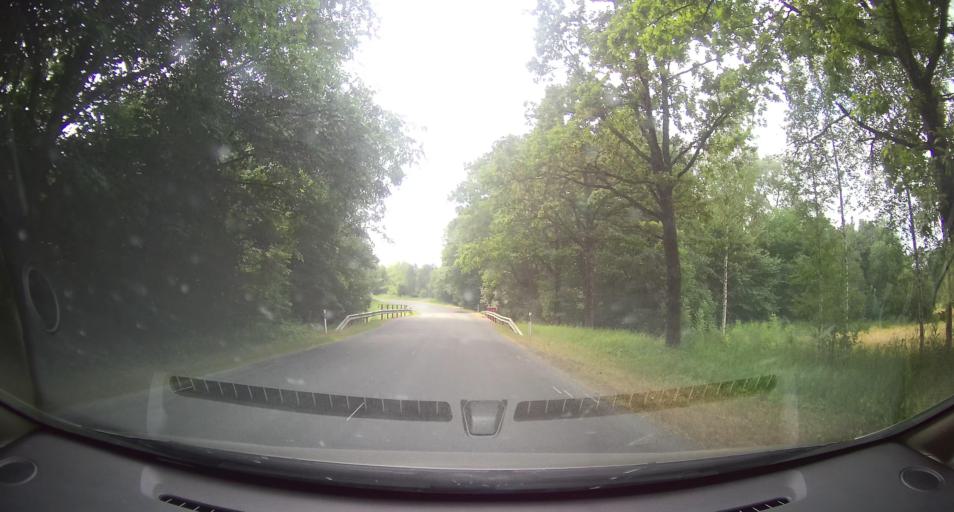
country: EE
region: Paernumaa
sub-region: Audru vald
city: Audru
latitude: 58.4455
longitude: 24.3087
